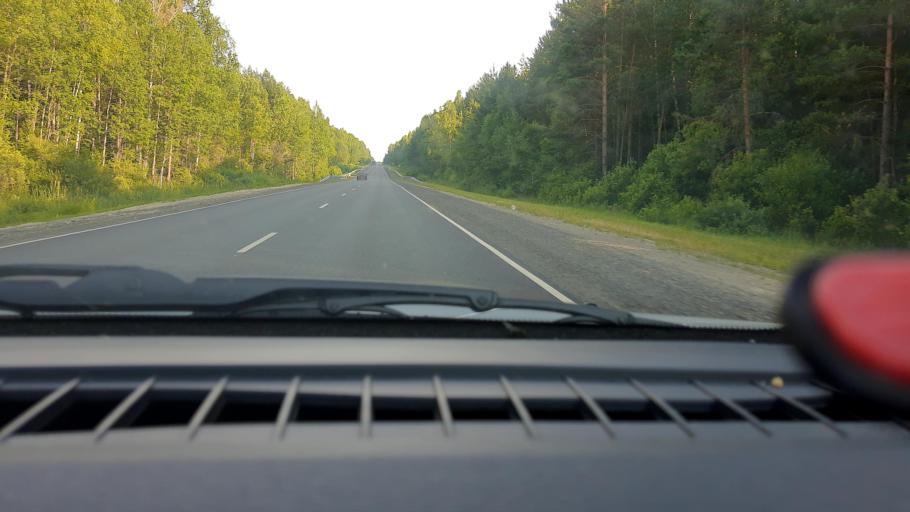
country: RU
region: Nizjnij Novgorod
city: Arzamas
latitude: 55.4419
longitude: 43.8913
